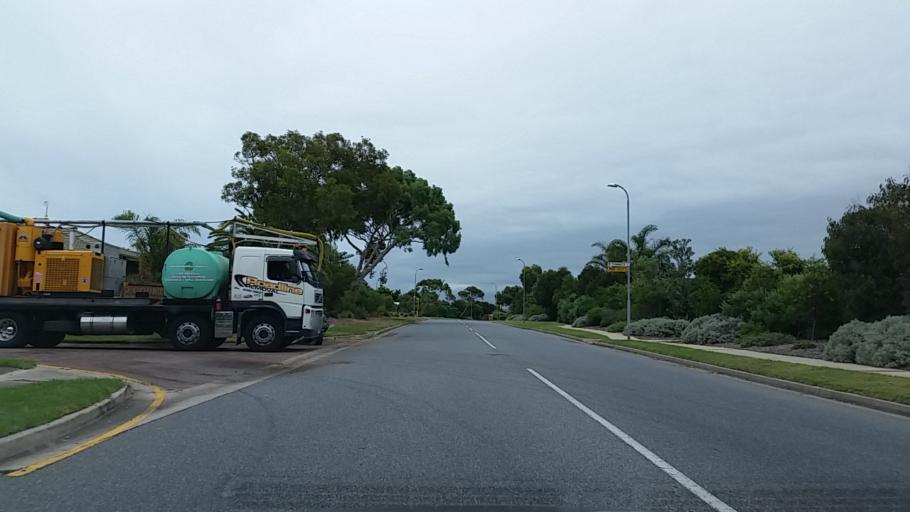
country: AU
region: South Australia
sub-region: Charles Sturt
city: West Lakes Shore
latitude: -34.8698
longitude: 138.4915
